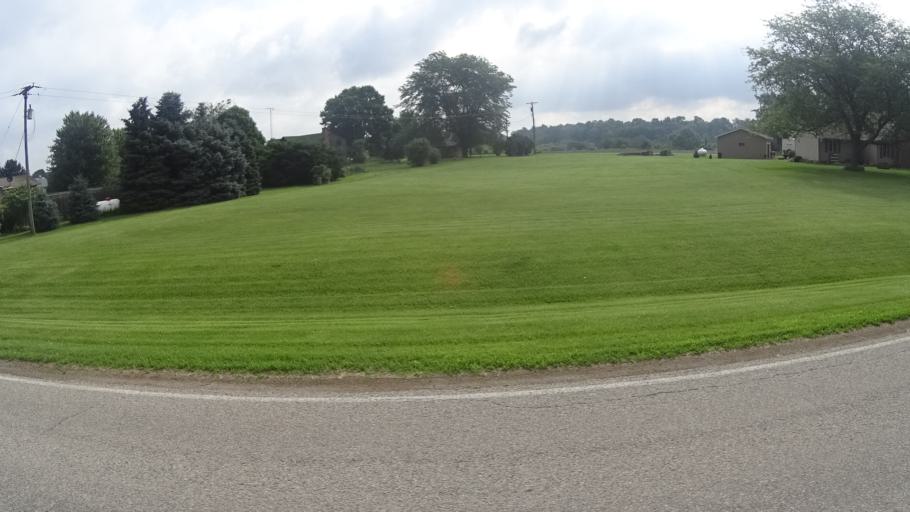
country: US
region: Ohio
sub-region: Erie County
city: Huron
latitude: 41.3523
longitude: -82.5166
